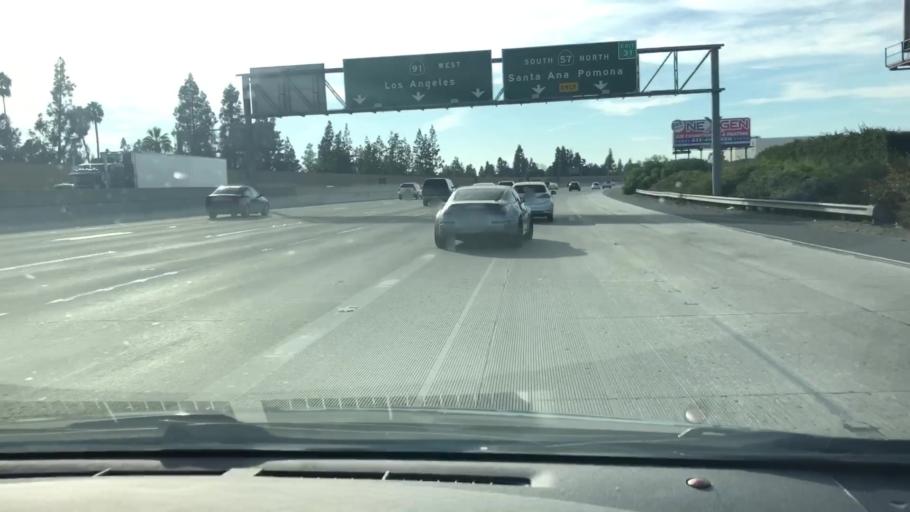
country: US
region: California
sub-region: Orange County
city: Placentia
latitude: 33.8468
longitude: -117.8611
